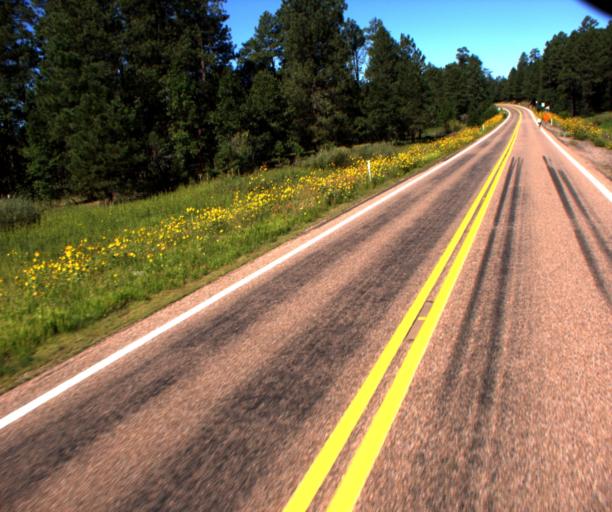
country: US
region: Arizona
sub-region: Navajo County
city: Pinetop-Lakeside
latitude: 34.0727
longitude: -109.8461
